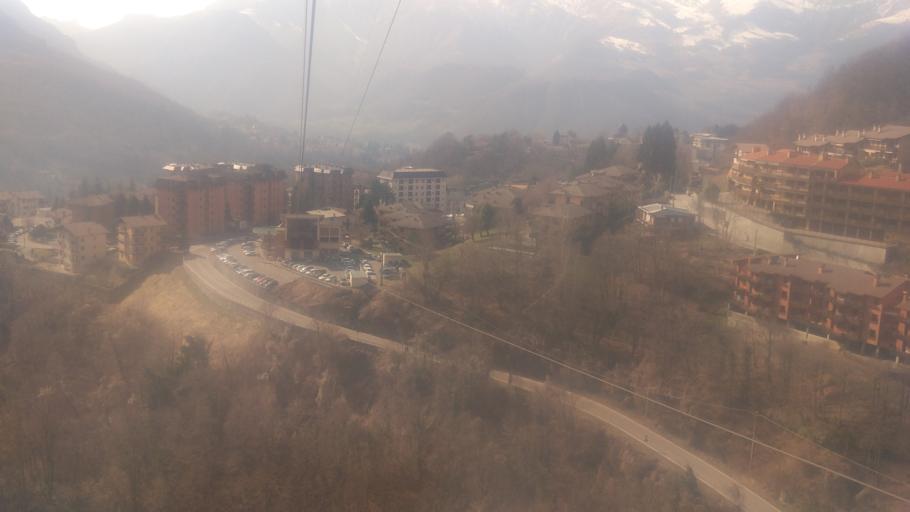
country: IT
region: Lombardy
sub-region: Provincia di Lecco
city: Moggio
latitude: 45.9300
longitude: 9.4953
